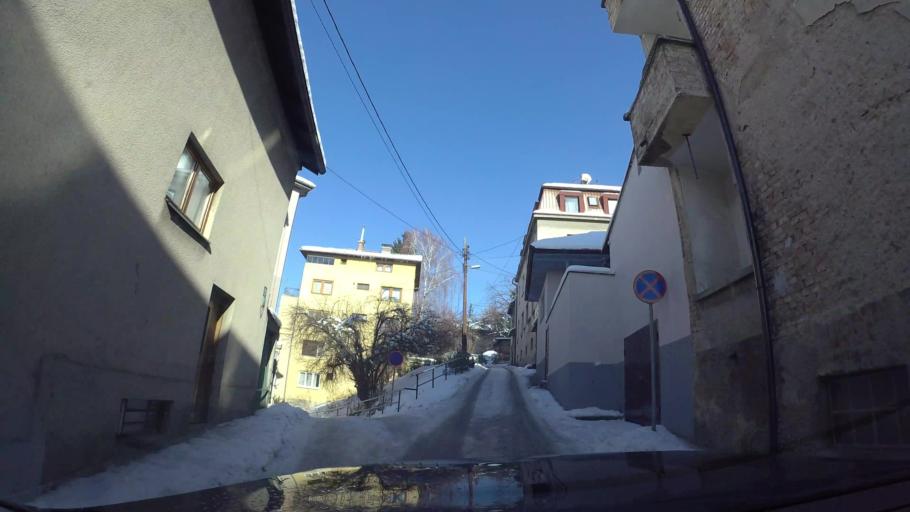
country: BA
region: Federation of Bosnia and Herzegovina
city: Kobilja Glava
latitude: 43.8630
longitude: 18.4210
